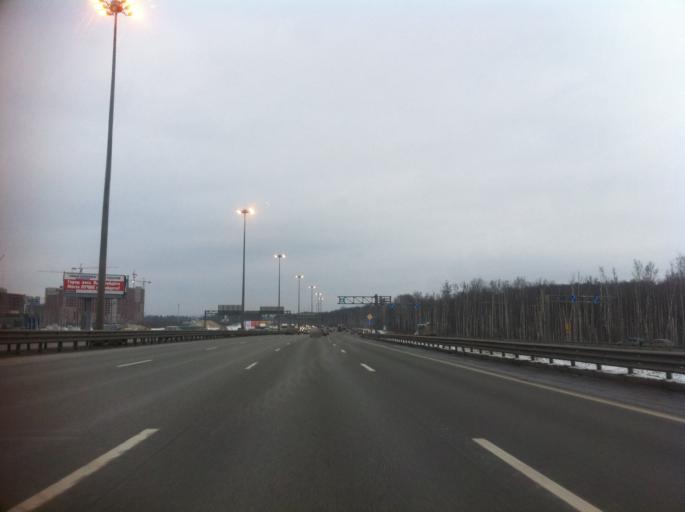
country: RU
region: Leningrad
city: Rybatskoye
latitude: 59.8865
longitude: 30.5253
